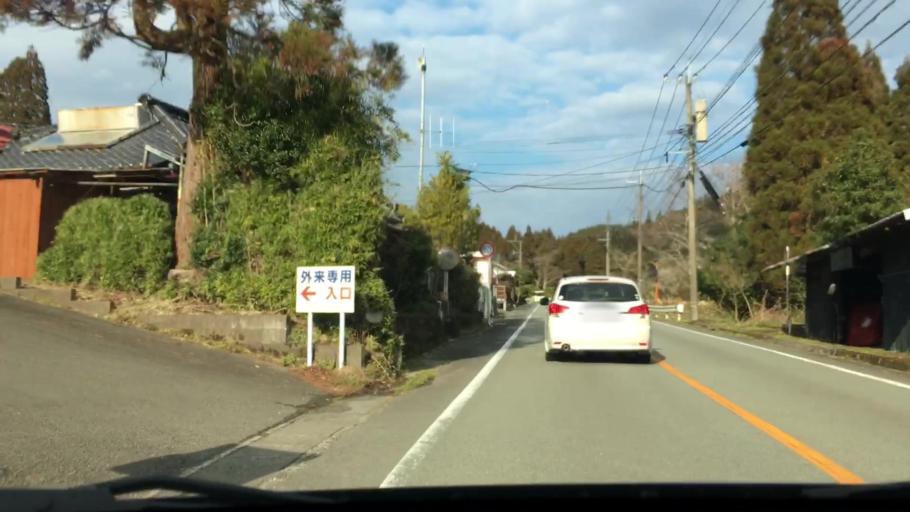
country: JP
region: Miyazaki
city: Nichinan
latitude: 31.7243
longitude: 131.3299
